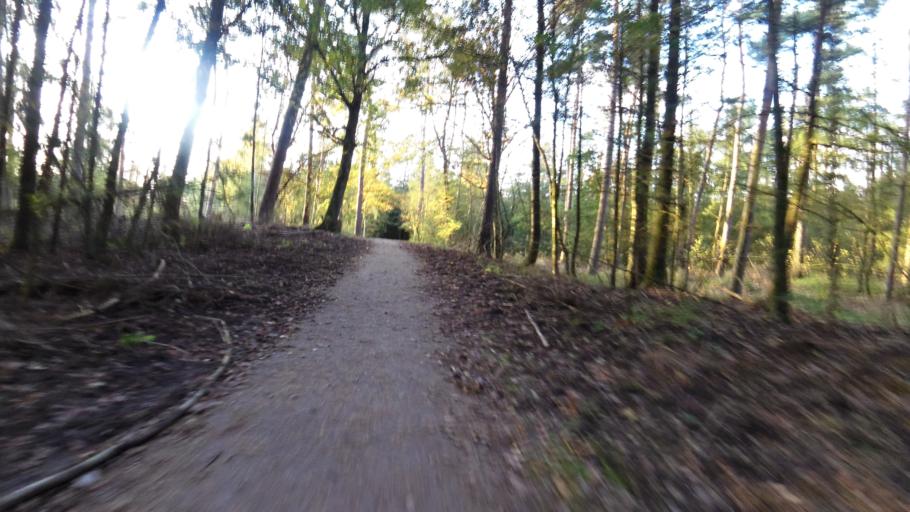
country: NL
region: Gelderland
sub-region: Gemeente Epe
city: Epe
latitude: 52.3707
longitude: 5.9627
